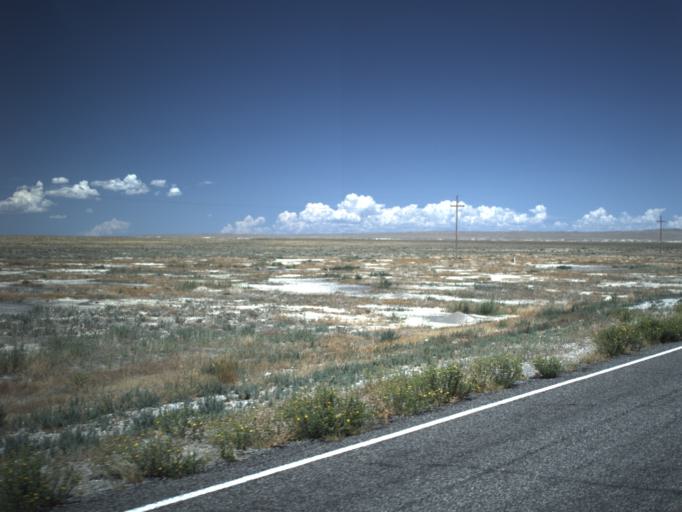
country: US
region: Utah
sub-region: Millard County
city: Delta
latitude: 39.0919
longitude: -113.1695
